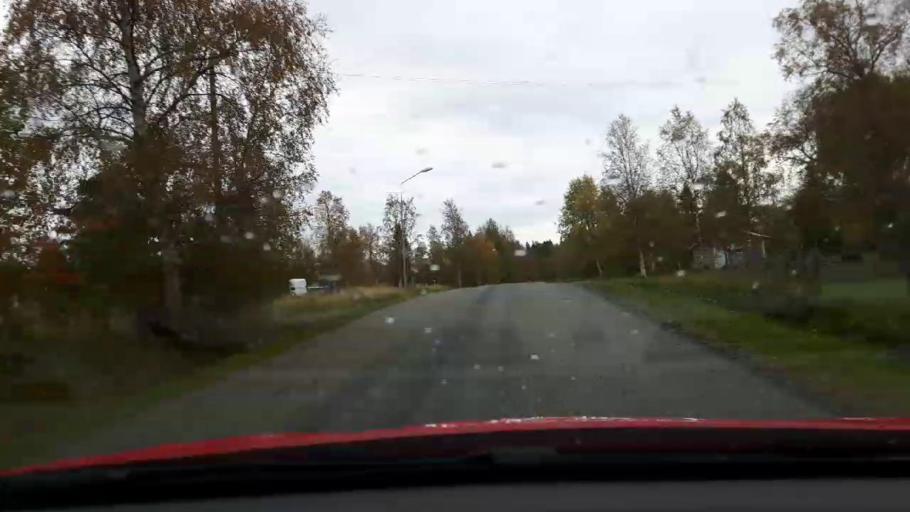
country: SE
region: Jaemtland
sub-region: Bergs Kommun
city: Hoverberg
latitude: 62.9388
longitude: 14.5050
